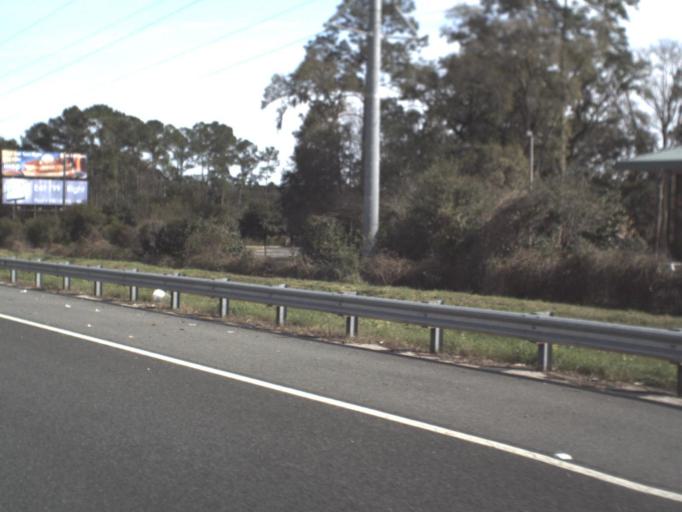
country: US
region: Florida
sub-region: Leon County
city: Tallahassee
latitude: 30.4781
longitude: -84.3517
